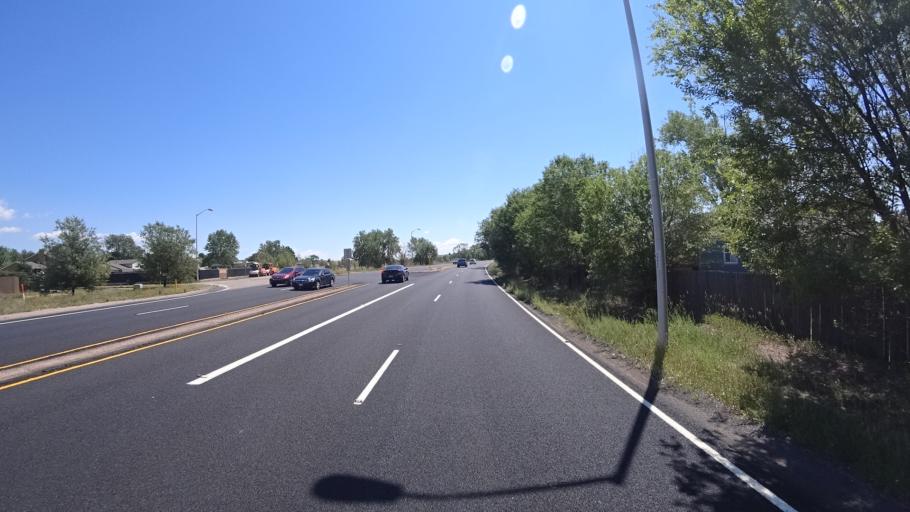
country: US
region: Colorado
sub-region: El Paso County
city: Stratmoor
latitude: 38.7888
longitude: -104.7445
